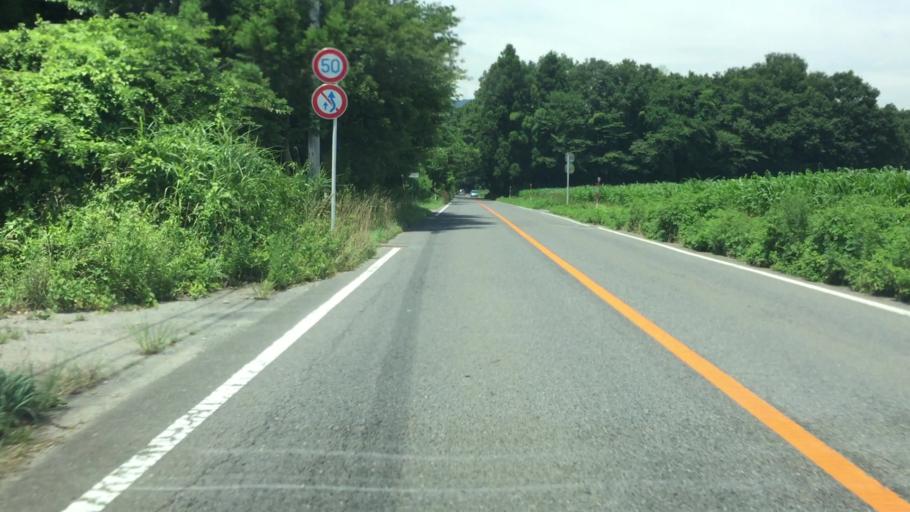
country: JP
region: Tochigi
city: Kuroiso
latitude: 37.0180
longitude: 139.9542
